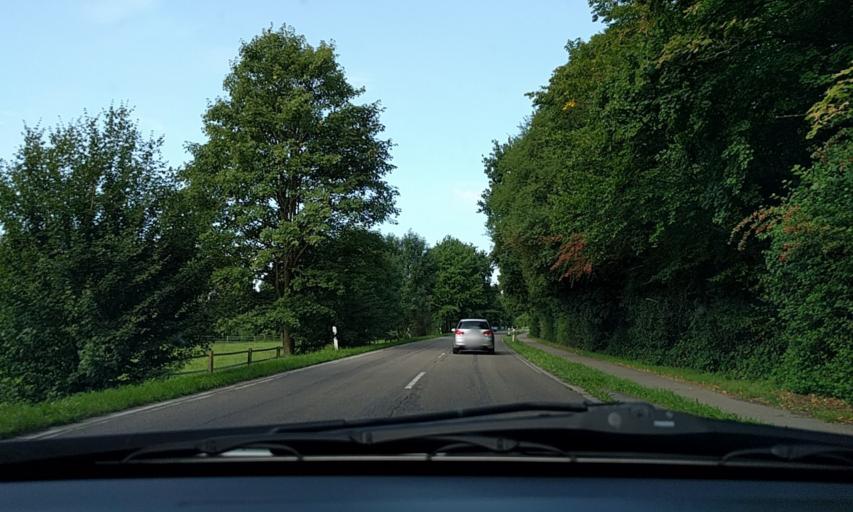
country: DE
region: North Rhine-Westphalia
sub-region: Regierungsbezirk Dusseldorf
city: Ratingen
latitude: 51.2852
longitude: 6.8111
